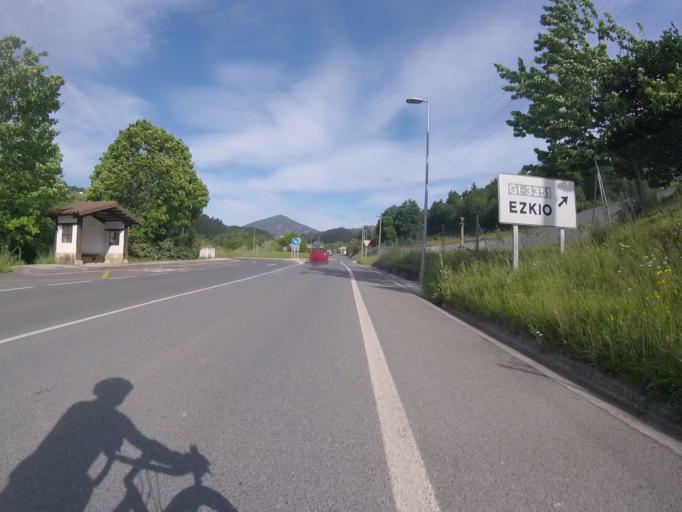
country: ES
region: Basque Country
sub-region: Provincia de Guipuzcoa
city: Zumarraga
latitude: 43.0754
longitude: -2.2904
